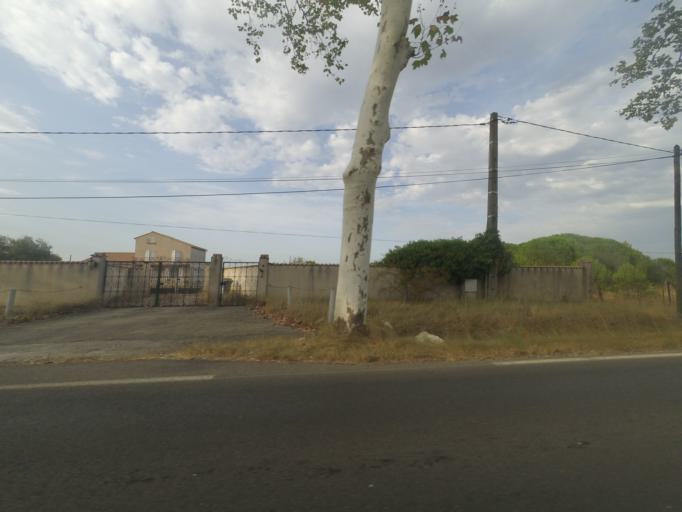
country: FR
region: Languedoc-Roussillon
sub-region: Departement de l'Herault
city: Boisseron
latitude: 43.7494
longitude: 4.0598
